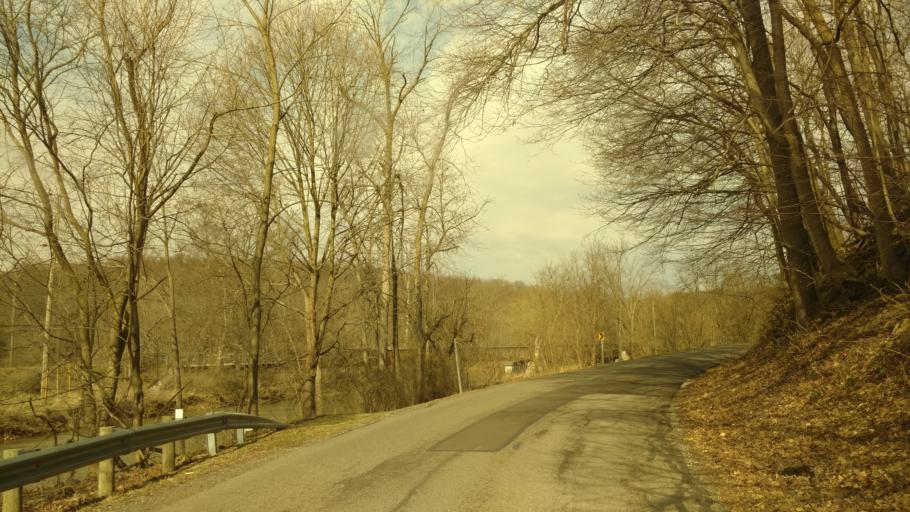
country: US
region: Ohio
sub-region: Sandusky County
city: Bellville
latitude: 40.6231
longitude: -82.5199
